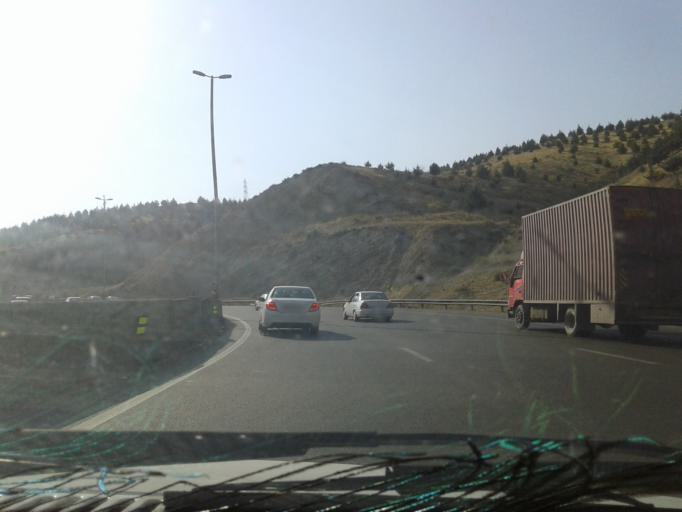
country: IR
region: Tehran
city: Tehran
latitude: 35.7358
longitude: 51.6747
